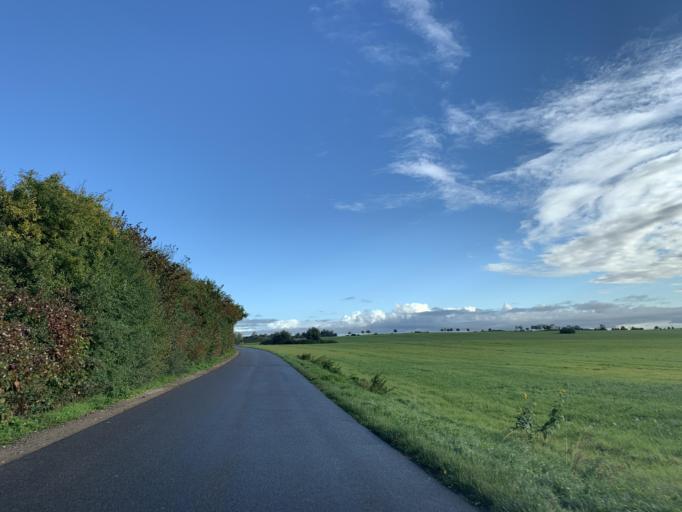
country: DE
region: Mecklenburg-Vorpommern
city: Blankensee
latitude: 53.4451
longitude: 13.2729
